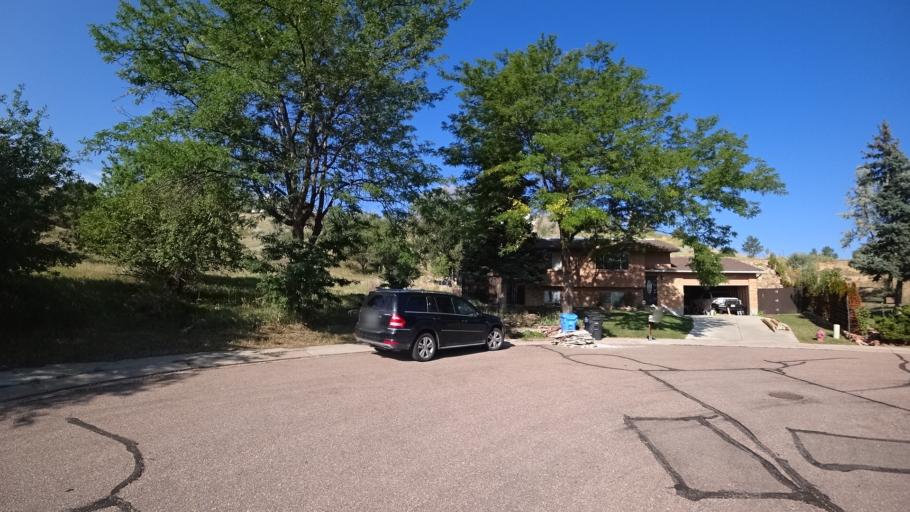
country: US
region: Colorado
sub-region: El Paso County
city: Colorado Springs
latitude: 38.8835
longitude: -104.8443
